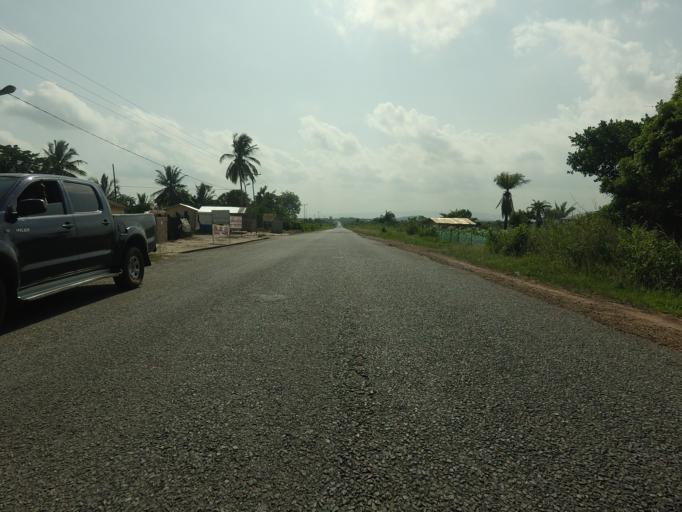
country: GH
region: Volta
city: Ho
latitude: 6.5686
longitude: 0.6040
